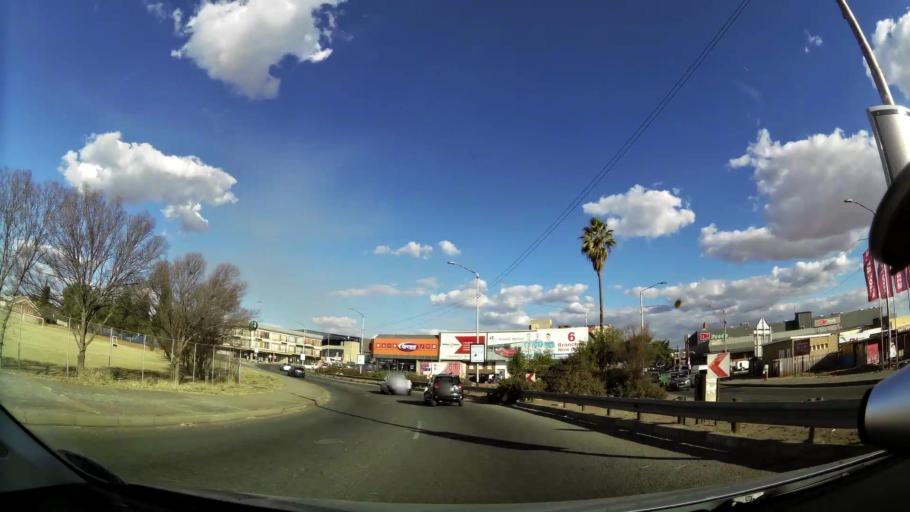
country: ZA
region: North-West
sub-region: Dr Kenneth Kaunda District Municipality
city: Klerksdorp
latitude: -26.8626
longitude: 26.6657
